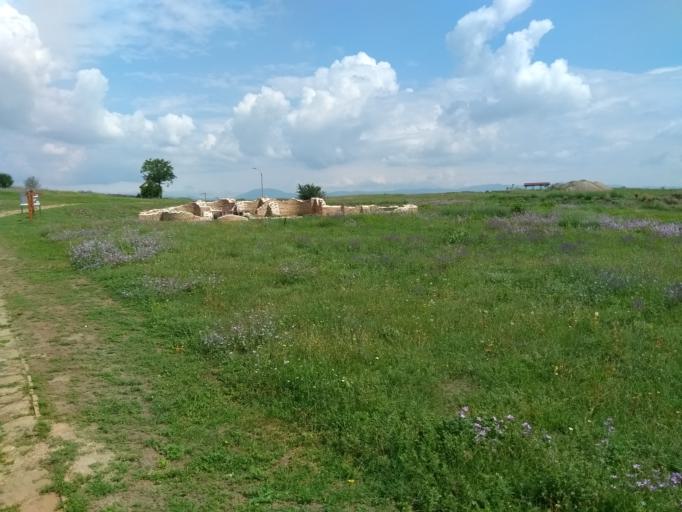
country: BG
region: Yambol
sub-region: Obshtina Yambol
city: Yambol
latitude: 42.5476
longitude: 26.4843
